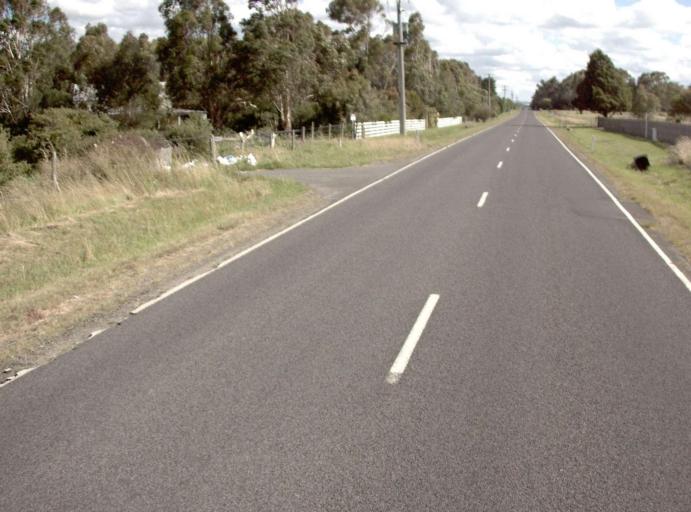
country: AU
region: Victoria
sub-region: Latrobe
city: Morwell
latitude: -38.2193
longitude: 146.3979
